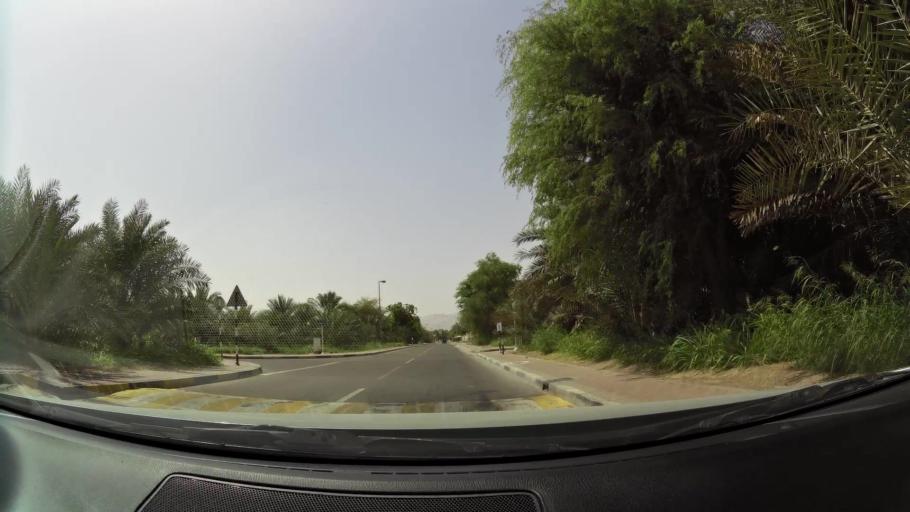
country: AE
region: Abu Dhabi
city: Al Ain
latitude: 24.1755
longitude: 55.7135
